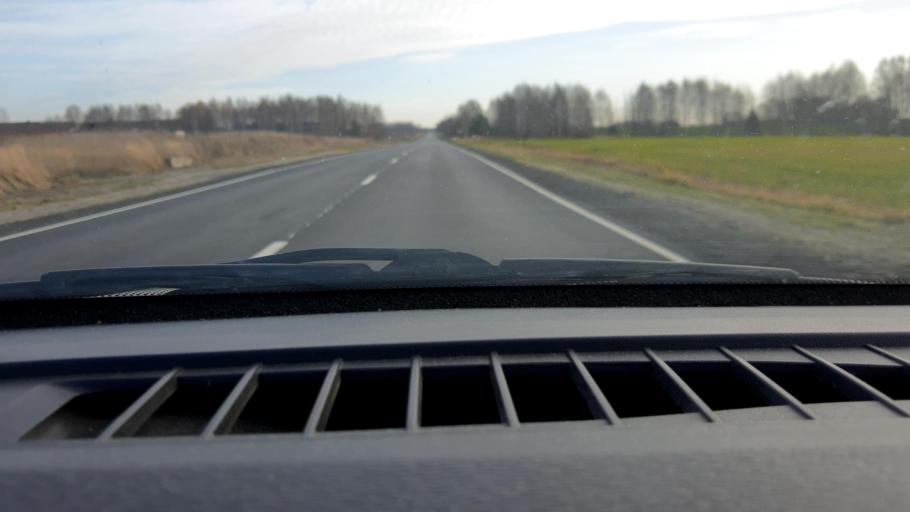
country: RU
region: Nizjnij Novgorod
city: Novaya Balakhna
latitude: 56.5842
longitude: 43.6783
